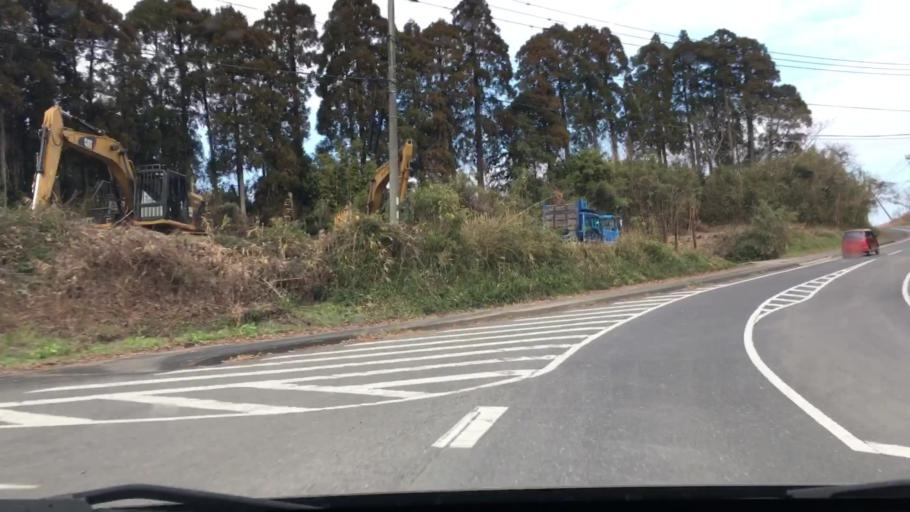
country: JP
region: Miyazaki
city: Kushima
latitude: 31.5043
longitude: 131.2393
